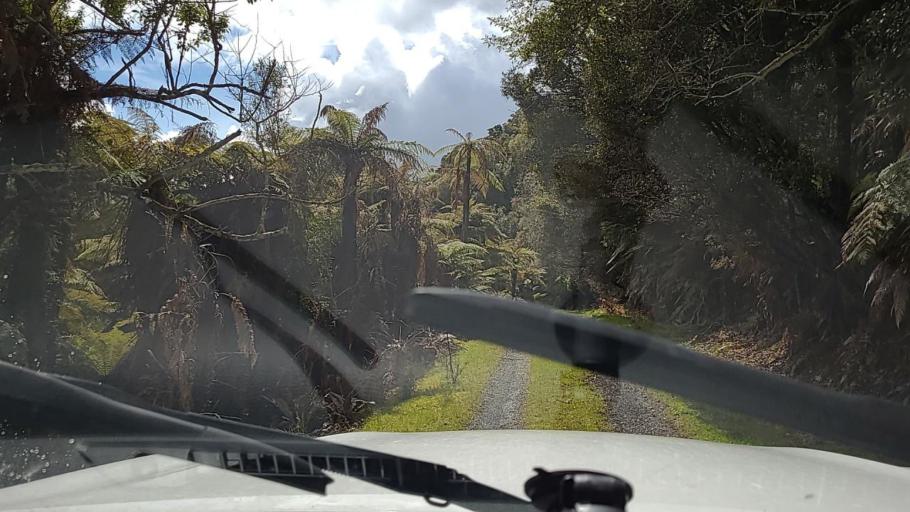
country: NZ
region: Bay of Plenty
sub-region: Opotiki District
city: Opotiki
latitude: -38.2049
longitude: 177.6145
